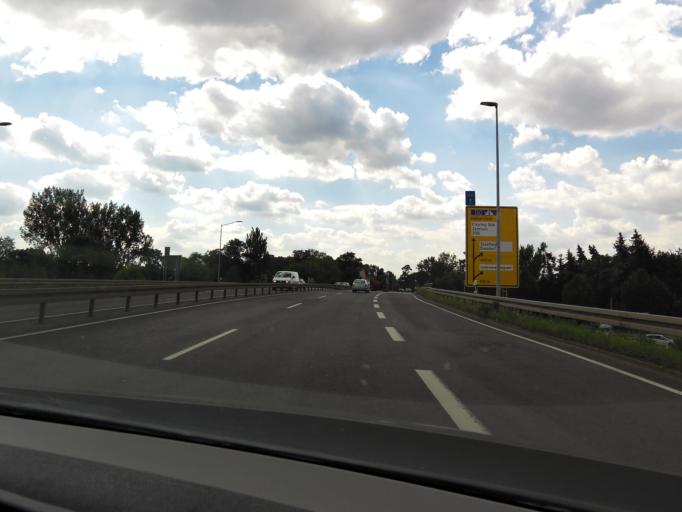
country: DE
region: Saxony-Anhalt
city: Neue Neustadt
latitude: 52.1412
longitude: 11.6289
